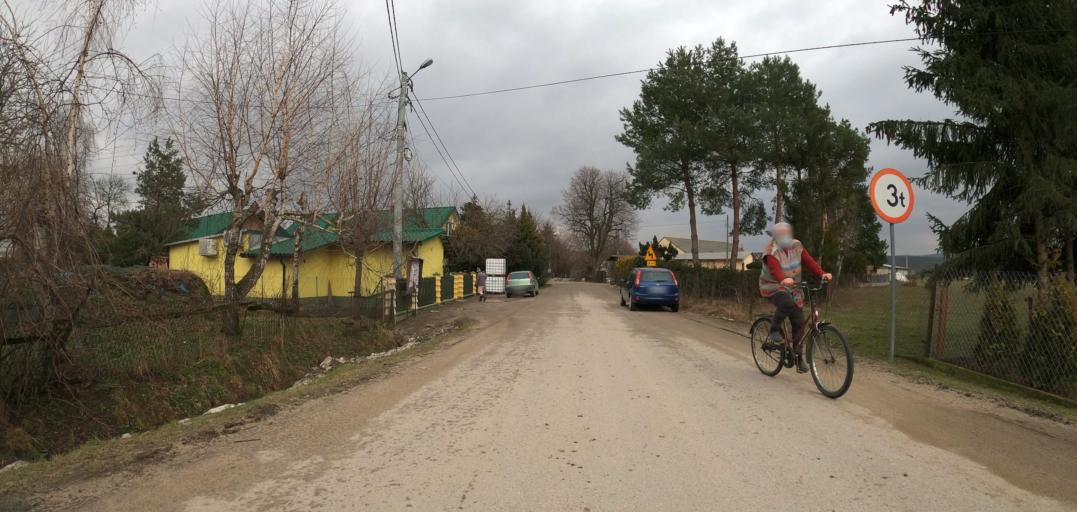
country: PL
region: Subcarpathian Voivodeship
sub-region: Powiat debicki
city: Pilzno
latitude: 49.9780
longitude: 21.3282
